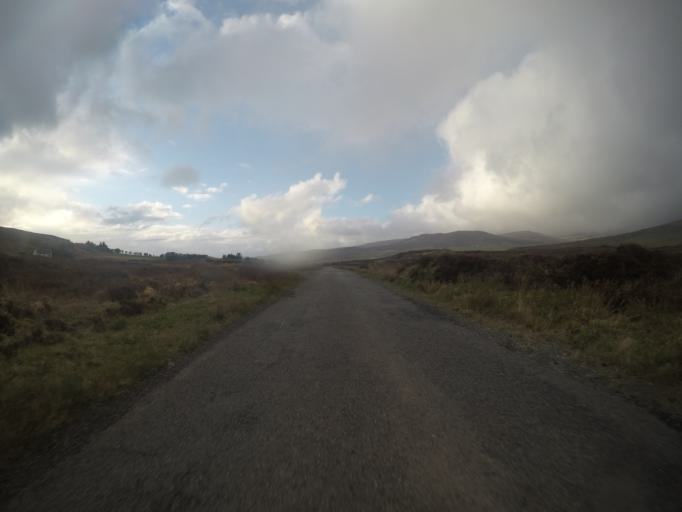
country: GB
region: Scotland
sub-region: Highland
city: Isle of Skye
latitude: 57.4634
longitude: -6.2970
